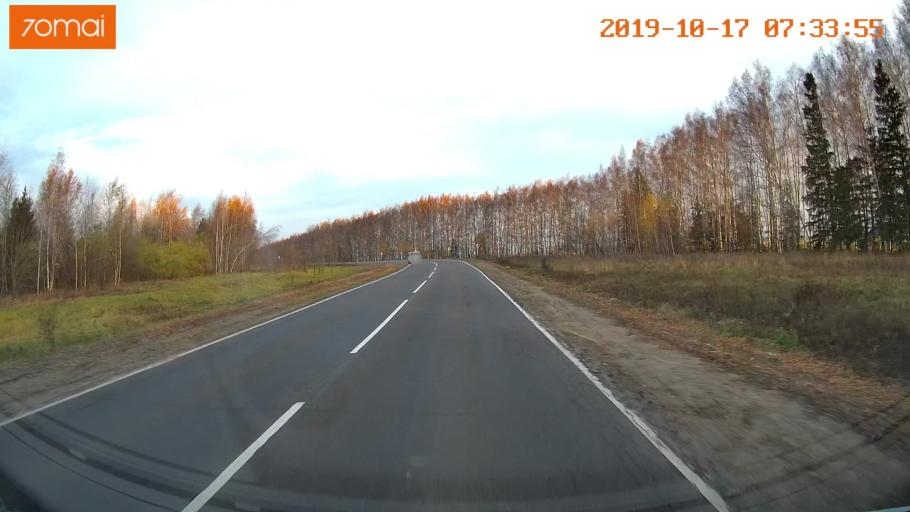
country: RU
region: Ivanovo
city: Gavrilov Posad
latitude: 56.4132
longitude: 39.9518
